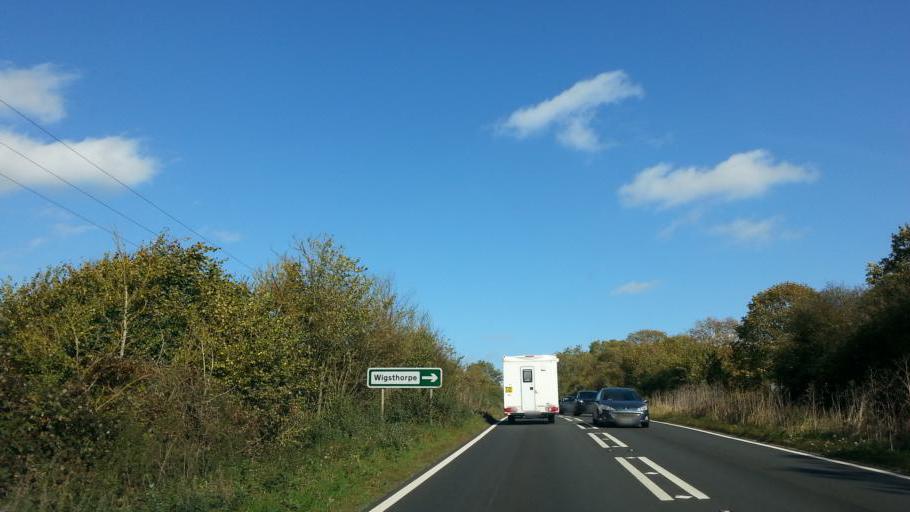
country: GB
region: England
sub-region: Northamptonshire
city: Oundle
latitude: 52.4362
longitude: -0.4772
